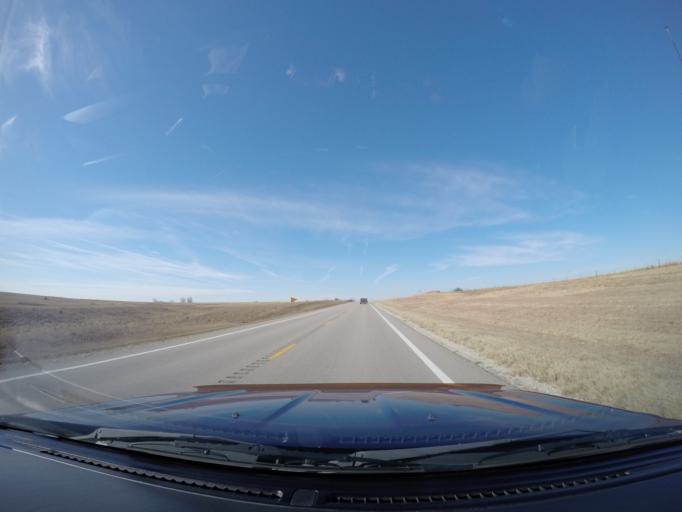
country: US
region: Kansas
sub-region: Clay County
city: Clay Center
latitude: 39.3786
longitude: -97.3440
